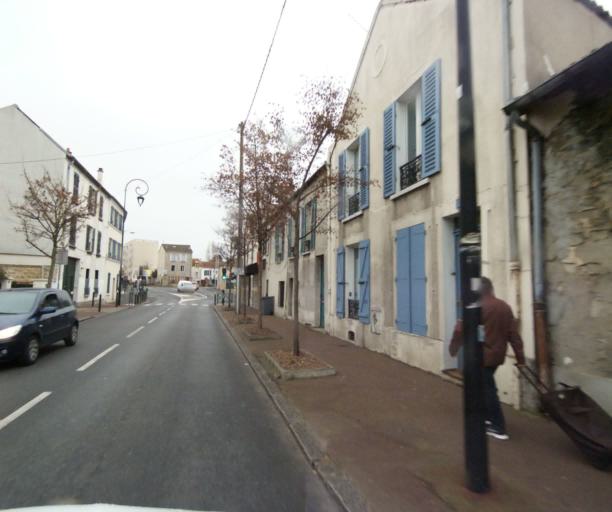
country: FR
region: Ile-de-France
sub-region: Departement des Hauts-de-Seine
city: Nanterre
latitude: 48.8919
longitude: 2.1997
